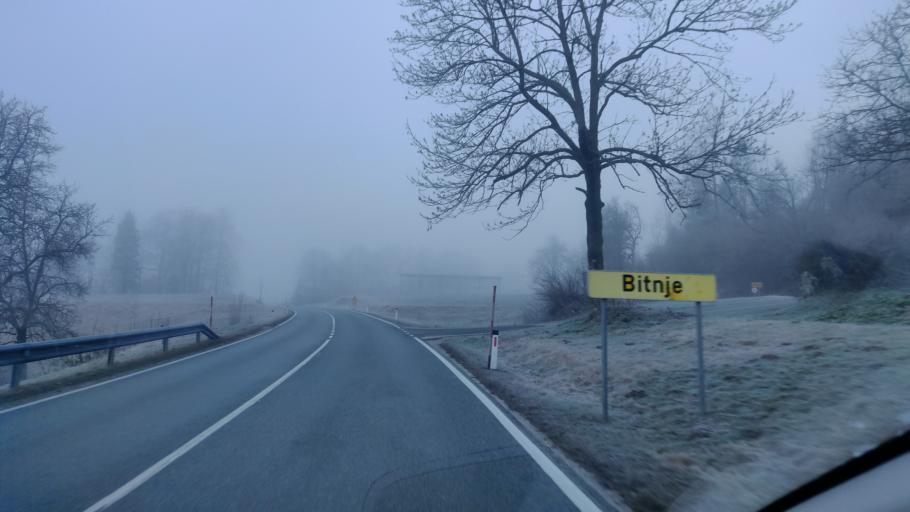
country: SI
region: Bohinj
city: Bohinjska Bistrica
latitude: 46.2829
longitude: 13.9653
